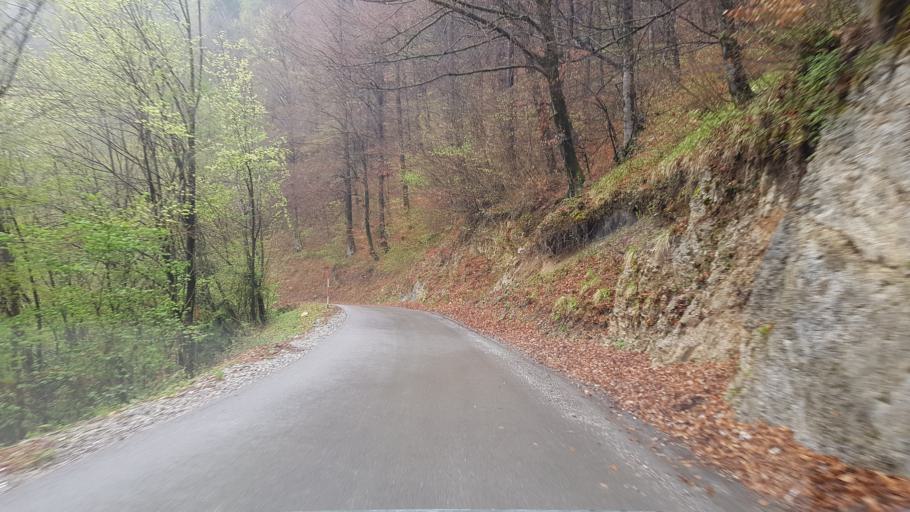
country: SI
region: Tolmin
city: Tolmin
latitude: 46.1454
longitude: 13.7873
